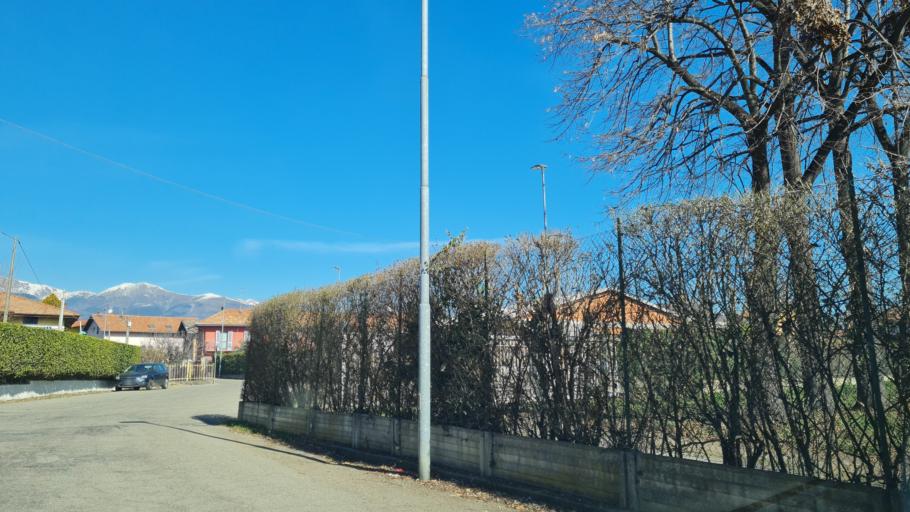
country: IT
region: Piedmont
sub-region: Provincia di Biella
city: Occhieppo Inferiore
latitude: 45.5438
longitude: 8.0163
